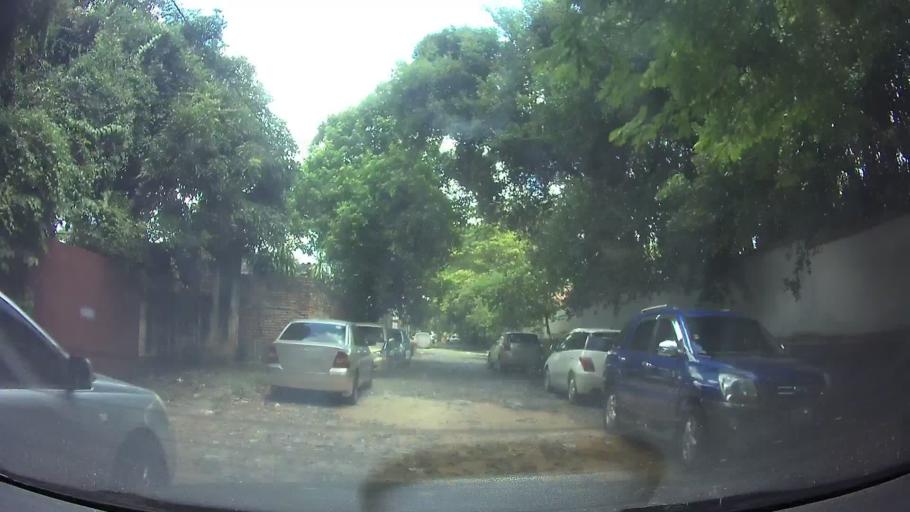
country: PY
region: Asuncion
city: Asuncion
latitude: -25.2944
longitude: -57.6012
